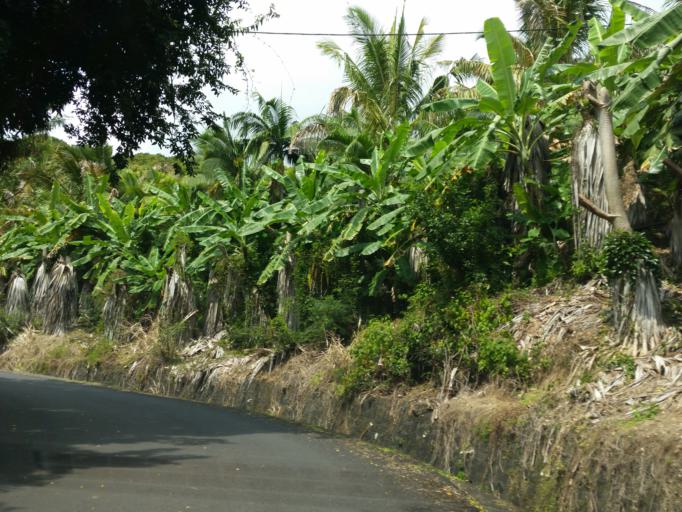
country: RE
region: Reunion
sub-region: Reunion
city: Sainte-Suzanne
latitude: -20.9256
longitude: 55.6059
